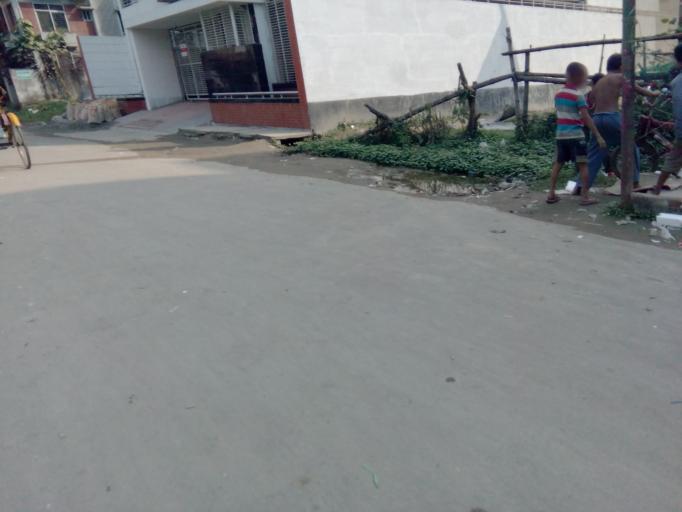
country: BD
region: Dhaka
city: Tungi
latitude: 23.8183
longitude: 90.4257
